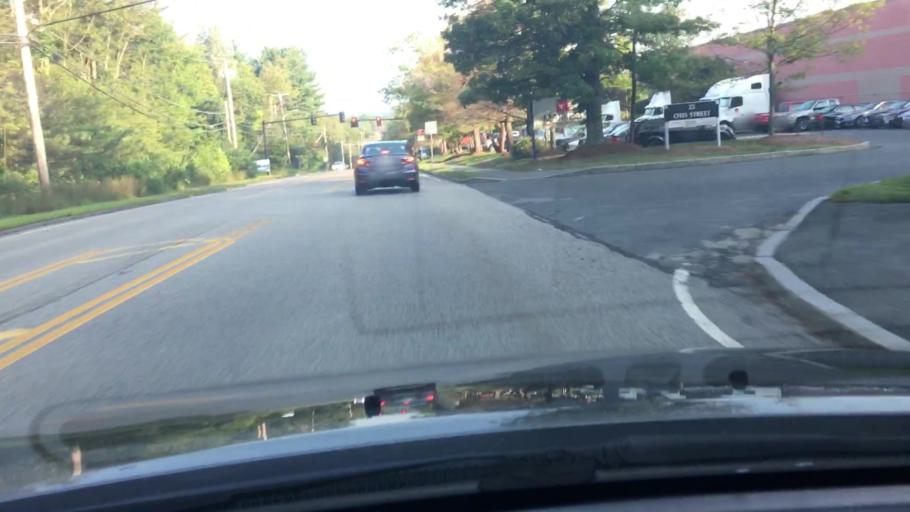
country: US
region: Massachusetts
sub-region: Worcester County
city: Westborough
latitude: 42.2715
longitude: -71.6423
